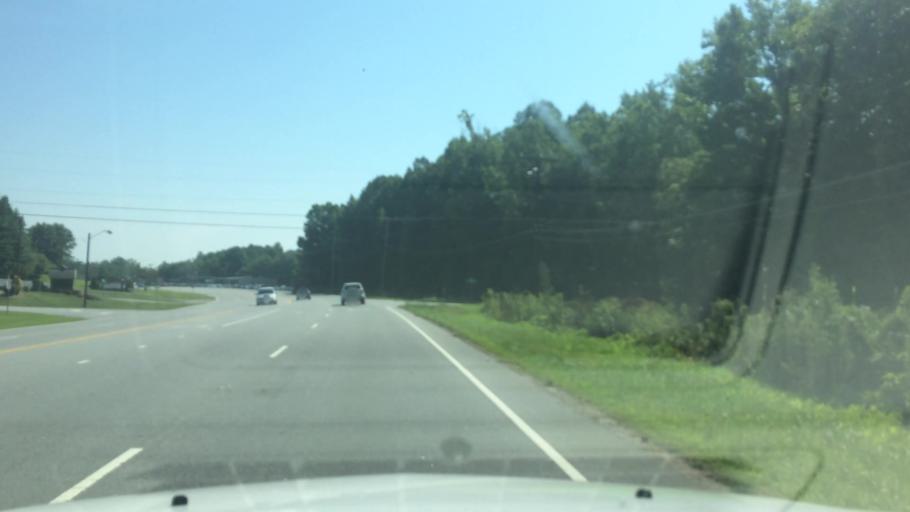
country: US
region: North Carolina
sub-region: Caldwell County
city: Lenoir
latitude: 35.9195
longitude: -81.5097
